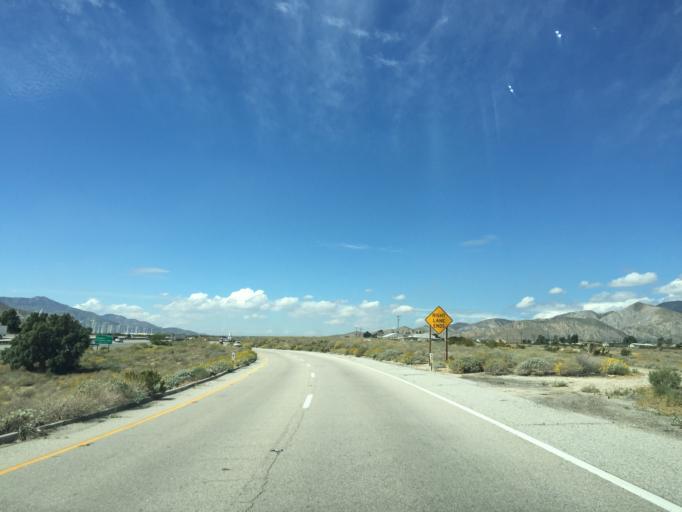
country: US
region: California
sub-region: Riverside County
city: Cabazon
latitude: 33.9231
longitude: -116.6799
